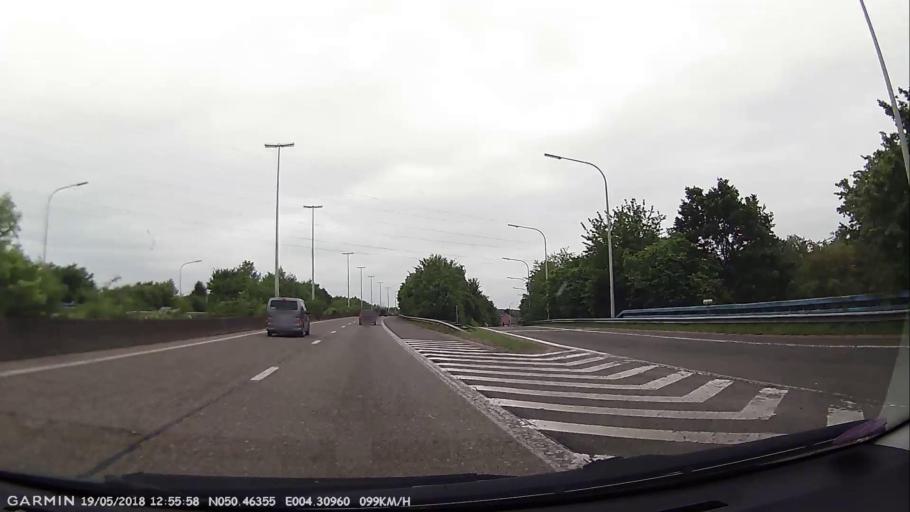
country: BE
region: Wallonia
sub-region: Province du Hainaut
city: Chapelle-lez-Herlaimont
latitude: 50.4639
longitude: 4.3101
